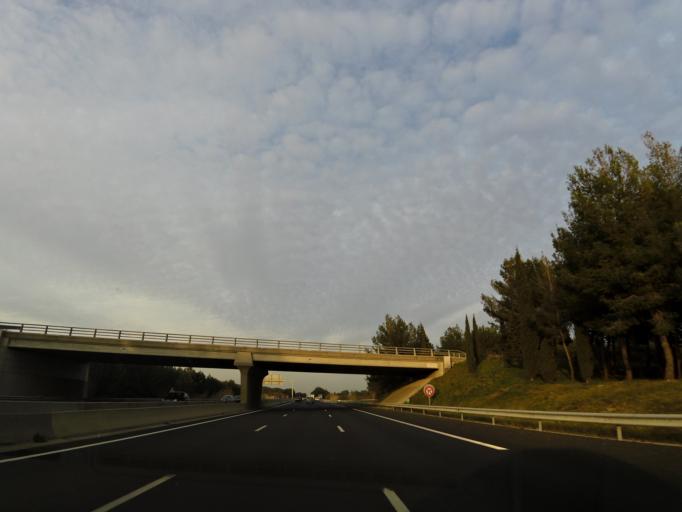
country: FR
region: Languedoc-Roussillon
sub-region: Departement de l'Herault
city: Lunel
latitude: 43.7022
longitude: 4.1158
